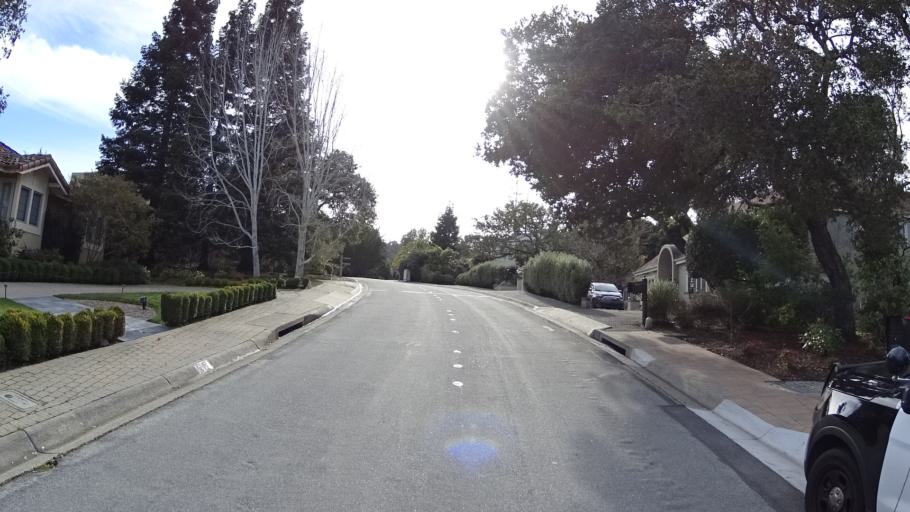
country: US
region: California
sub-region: San Mateo County
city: Burlingame
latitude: 37.5654
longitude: -122.3623
